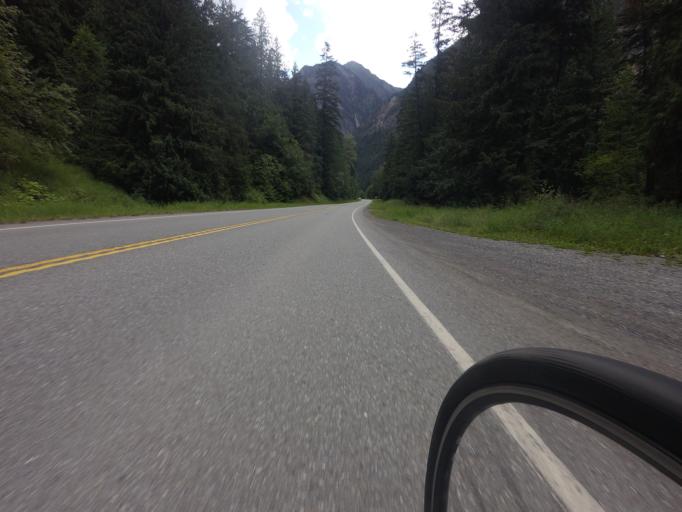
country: CA
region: British Columbia
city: Lillooet
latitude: 50.6259
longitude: -122.0983
